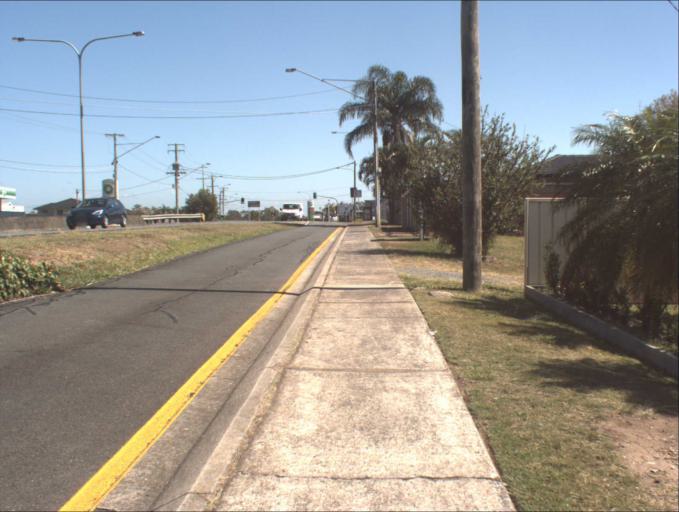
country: AU
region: Queensland
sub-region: Logan
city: Rochedale South
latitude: -27.5994
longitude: 153.1100
